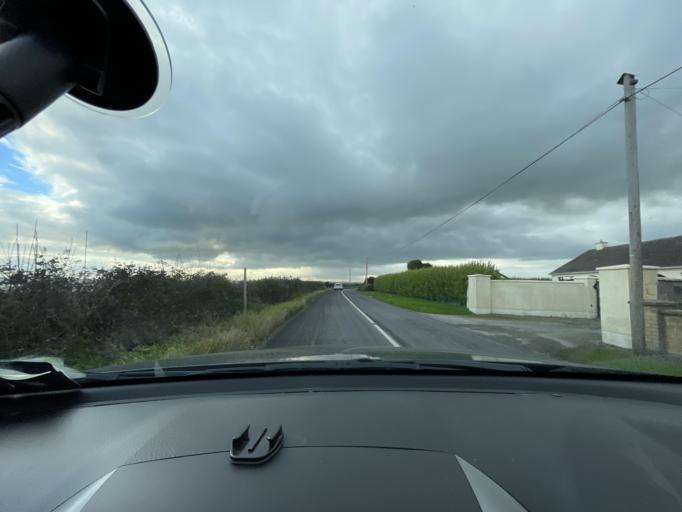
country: IE
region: Leinster
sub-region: Lu
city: Clogherhead
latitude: 53.7747
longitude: -6.2476
